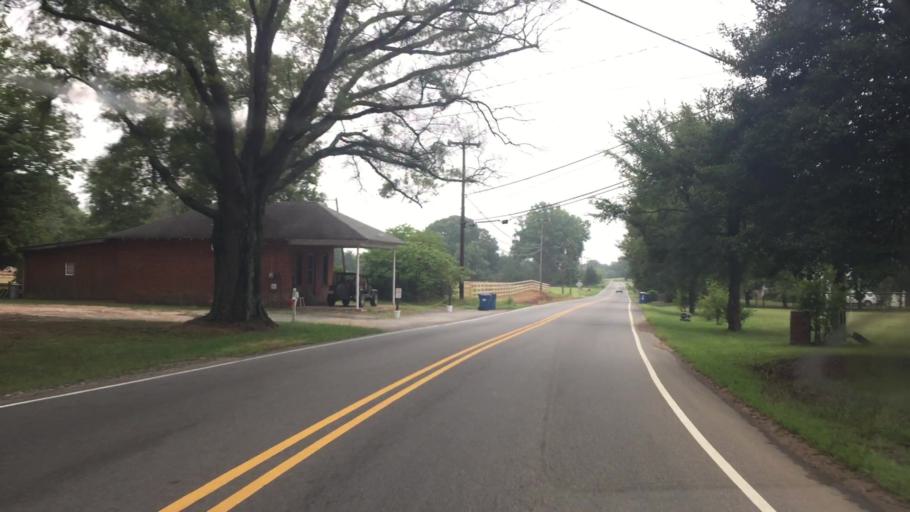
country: US
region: North Carolina
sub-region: Rowan County
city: Enochville
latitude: 35.4603
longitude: -80.7324
